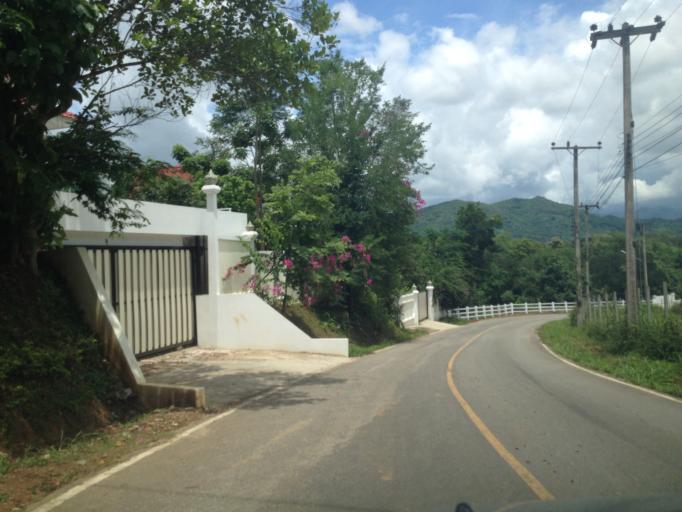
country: TH
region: Chiang Mai
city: Hang Dong
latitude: 18.7175
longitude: 98.8869
